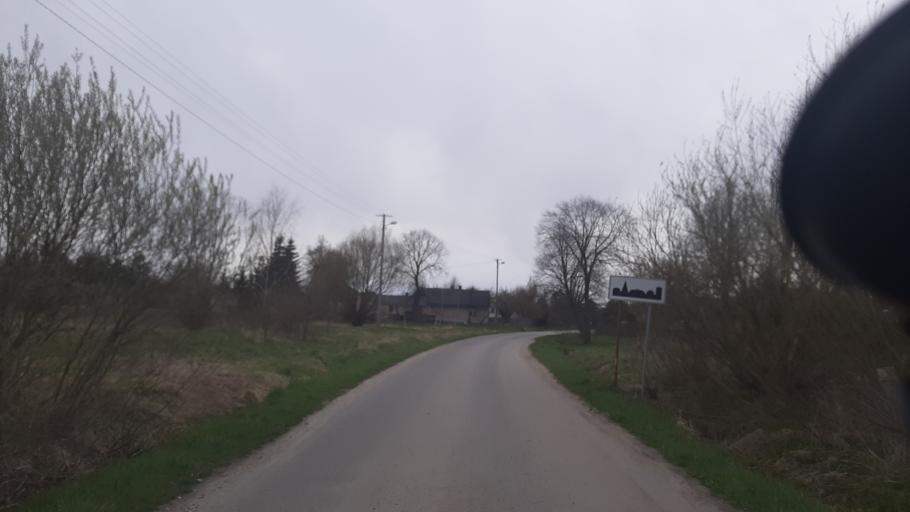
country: PL
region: Lublin Voivodeship
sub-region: Powiat lubelski
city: Niemce
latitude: 51.3858
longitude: 22.5626
